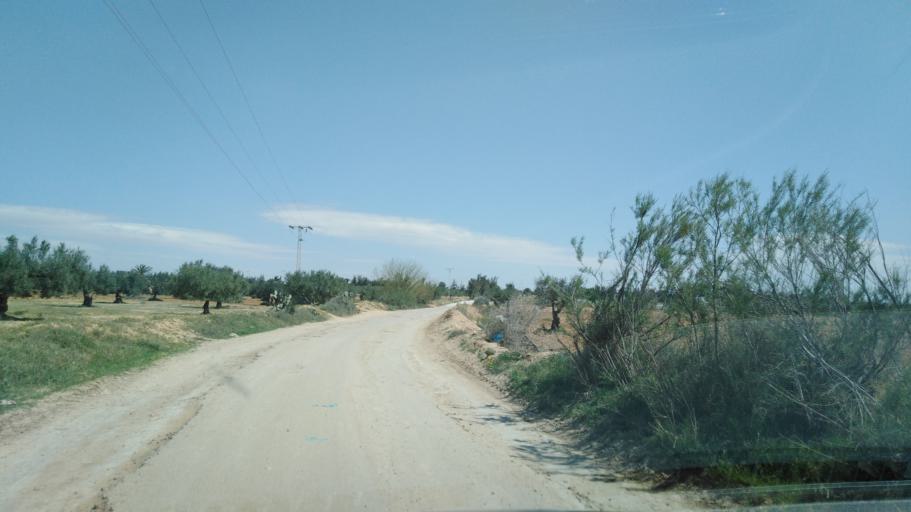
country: TN
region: Safaqis
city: Sfax
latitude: 34.7531
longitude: 10.5281
